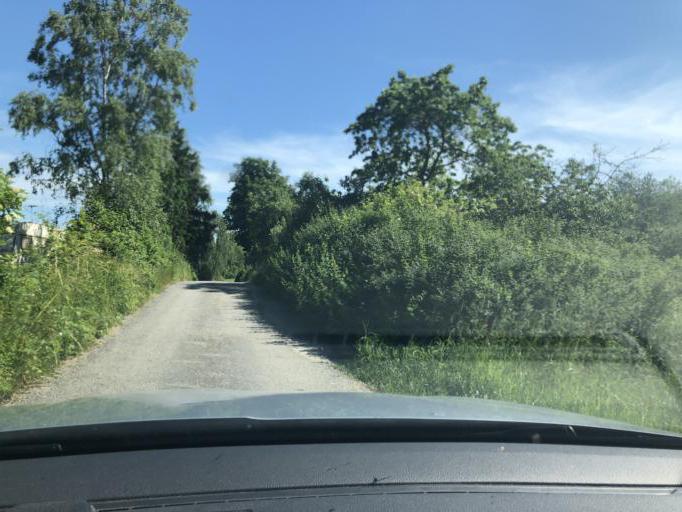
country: SE
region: Blekinge
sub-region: Karlshamns Kommun
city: Morrum
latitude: 56.1831
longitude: 14.7005
